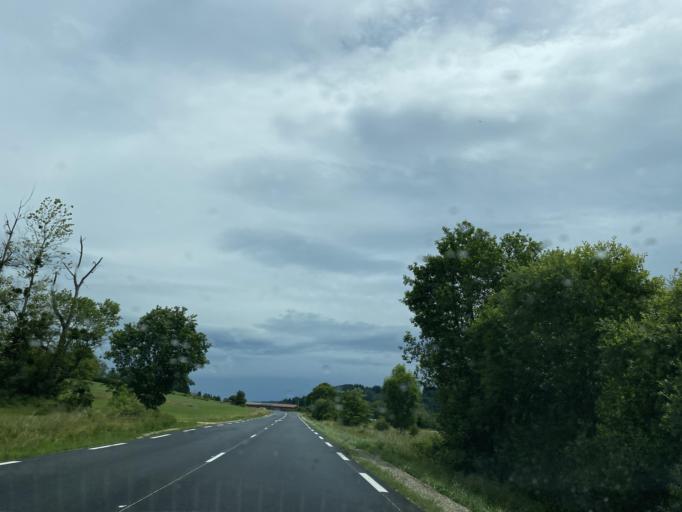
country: FR
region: Rhone-Alpes
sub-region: Departement de la Loire
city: Noiretable
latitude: 45.8092
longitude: 3.7875
